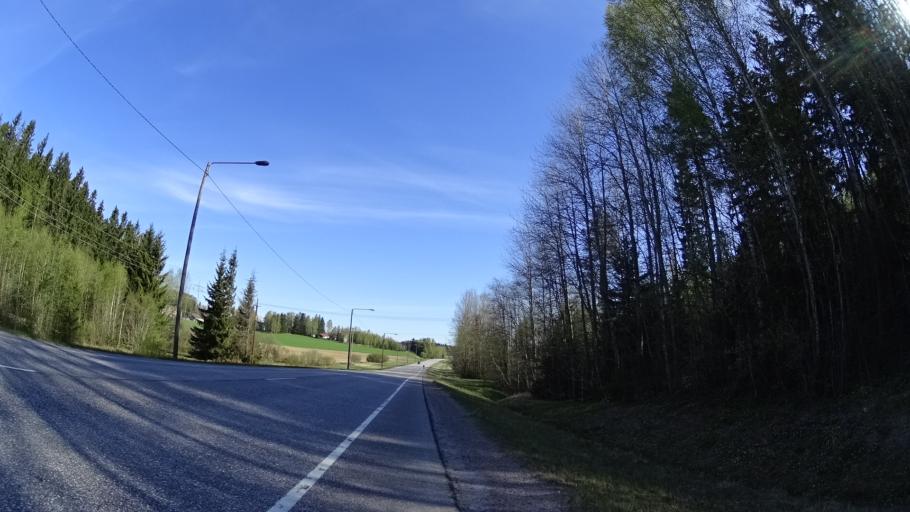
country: FI
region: Uusimaa
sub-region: Helsinki
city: Nurmijaervi
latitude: 60.3888
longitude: 24.8088
